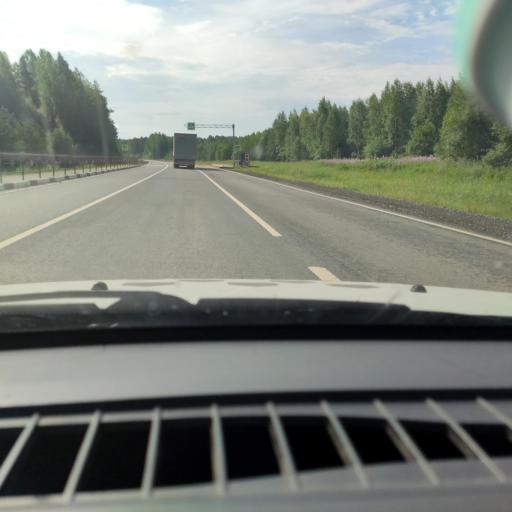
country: RU
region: Perm
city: Siva
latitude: 58.4394
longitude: 54.4323
